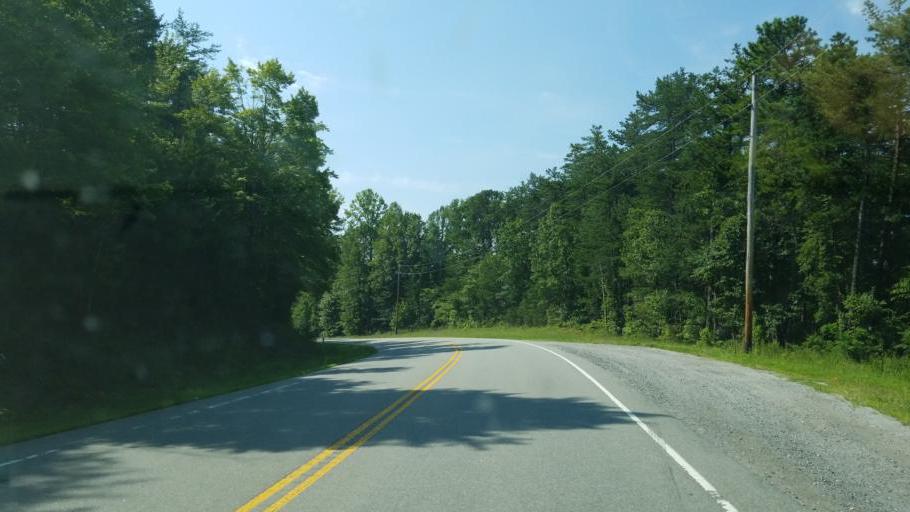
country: US
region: North Carolina
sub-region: Burke County
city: Glen Alpine
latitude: 35.9096
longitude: -81.8079
